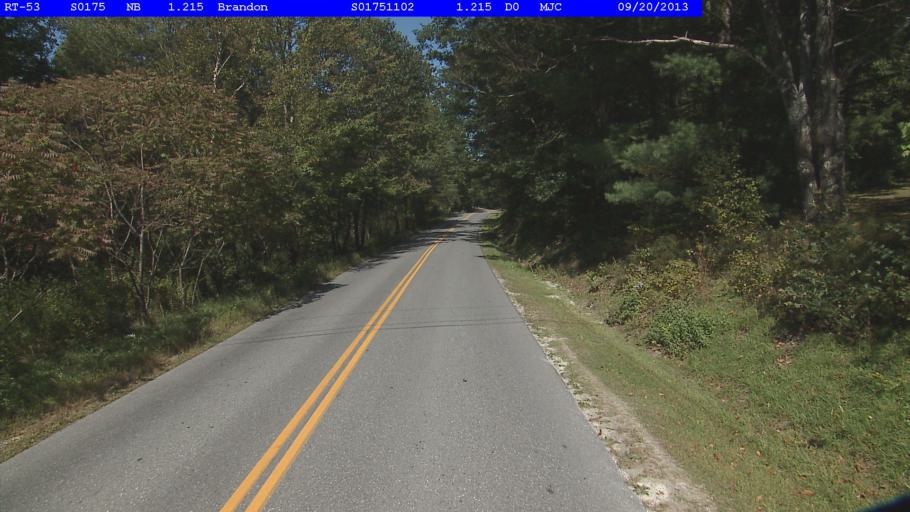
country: US
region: Vermont
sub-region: Rutland County
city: Brandon
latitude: 43.8443
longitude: -73.0569
